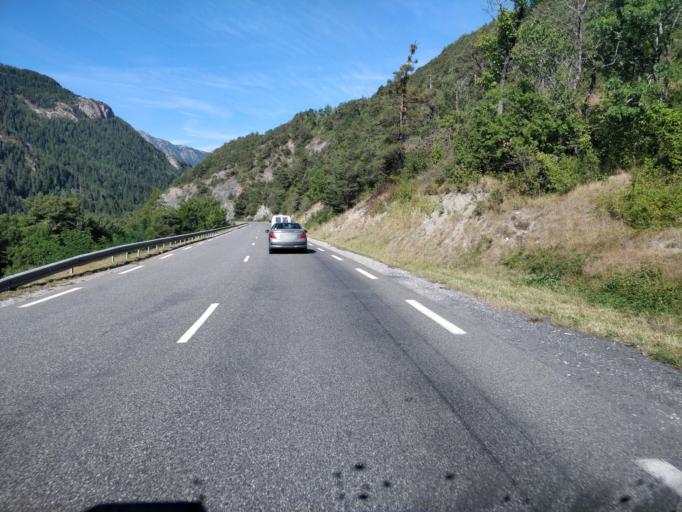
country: FR
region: Provence-Alpes-Cote d'Azur
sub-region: Departement des Alpes-de-Haute-Provence
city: Barcelonnette
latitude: 44.3998
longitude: 6.5417
